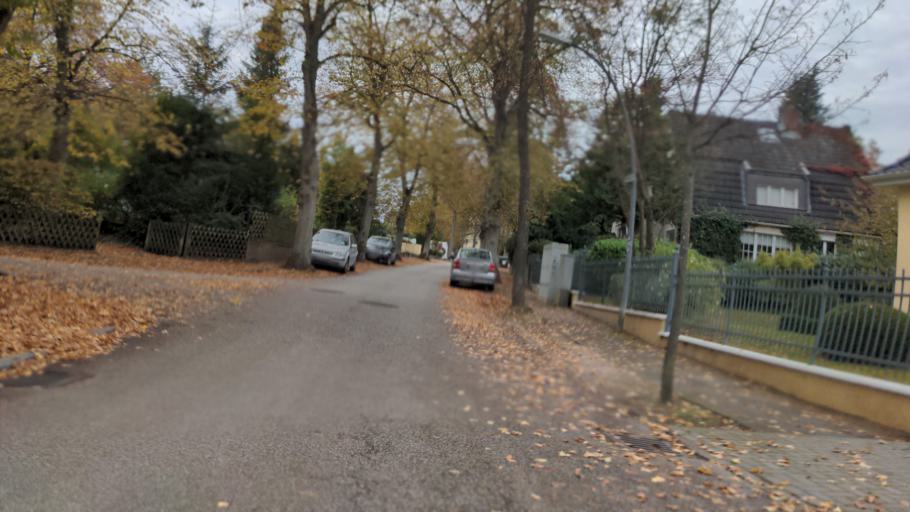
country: DE
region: Schleswig-Holstein
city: Bad Schwartau
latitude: 53.9076
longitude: 10.6801
